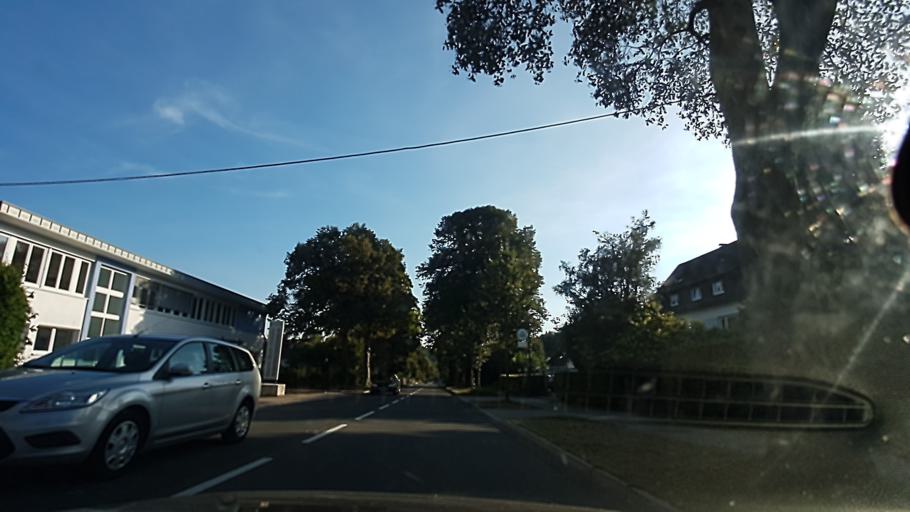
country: DE
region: North Rhine-Westphalia
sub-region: Regierungsbezirk Koln
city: Marienheide
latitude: 51.0691
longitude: 7.5590
